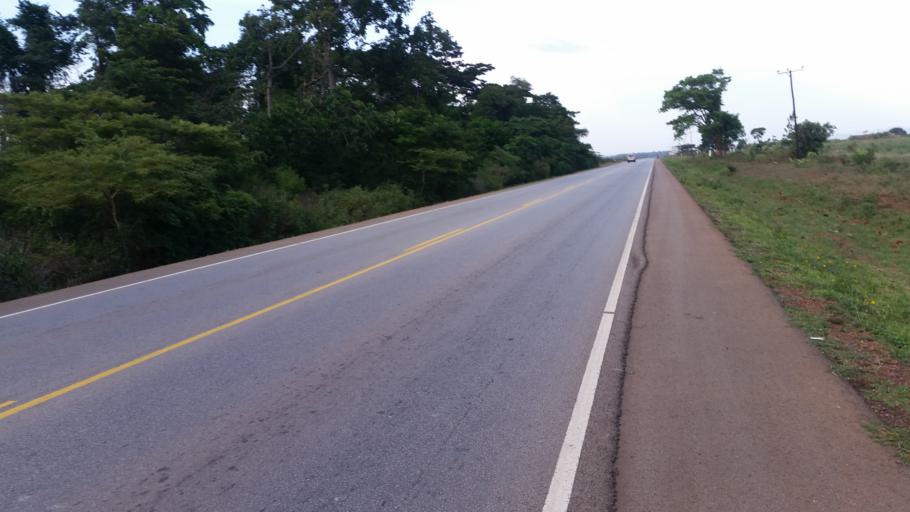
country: UG
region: Eastern Region
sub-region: Busia District
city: Busia
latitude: 0.5470
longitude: 34.0175
